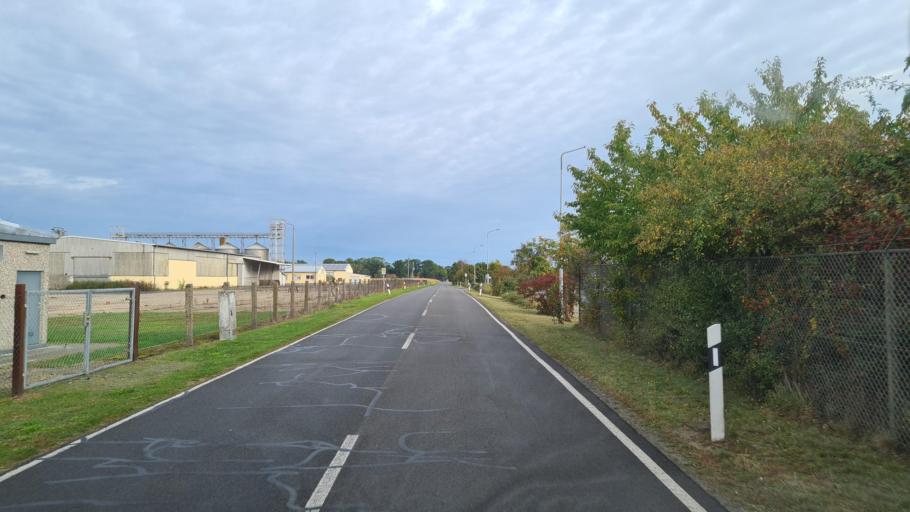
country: DE
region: Brandenburg
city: Kasel-Golzig
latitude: 51.9266
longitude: 13.7082
